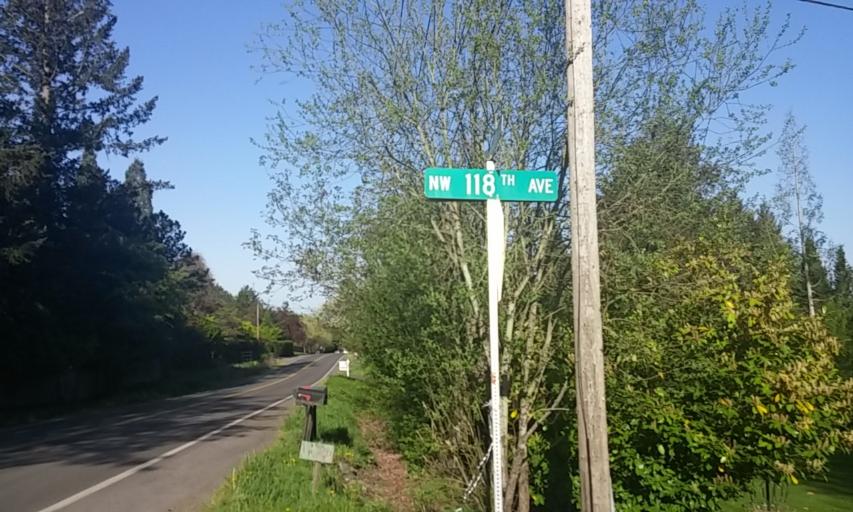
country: US
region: Oregon
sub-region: Washington County
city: Cedar Mill
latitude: 45.5483
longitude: -122.7981
